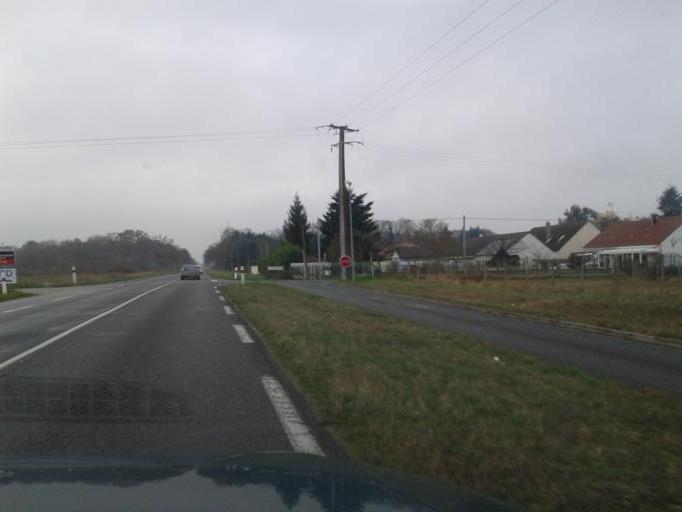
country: FR
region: Centre
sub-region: Departement du Loiret
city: Dry
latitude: 47.7888
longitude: 1.7146
